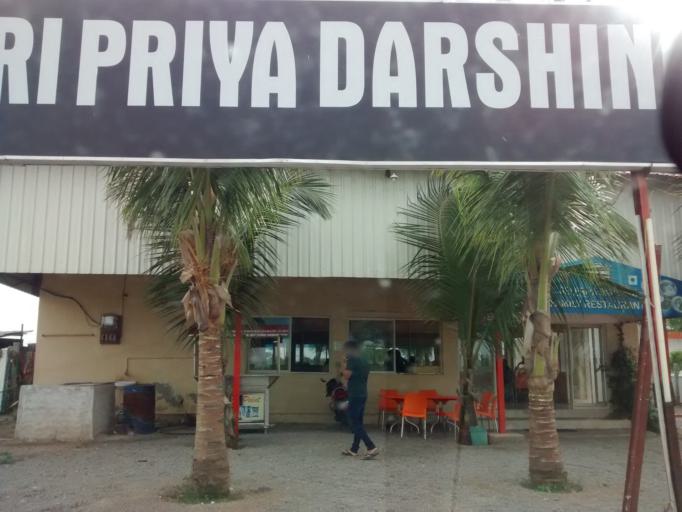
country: IN
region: Telangana
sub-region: Mahbubnagar
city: Gadwal
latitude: 16.0495
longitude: 77.9165
